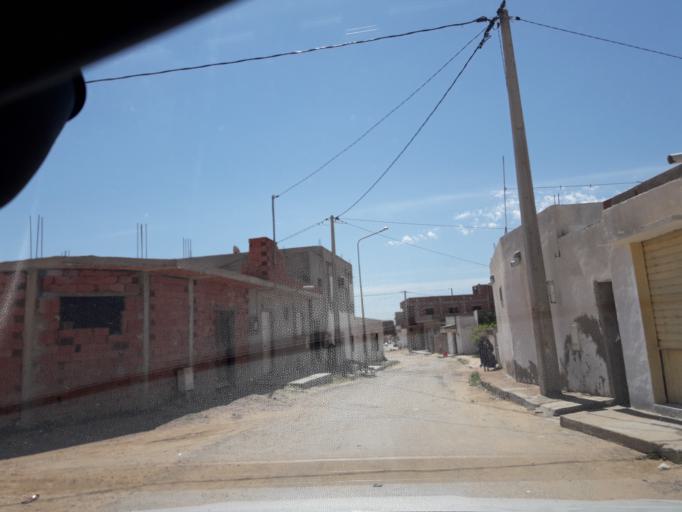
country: TN
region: Safaqis
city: Sfax
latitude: 34.7408
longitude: 10.5208
